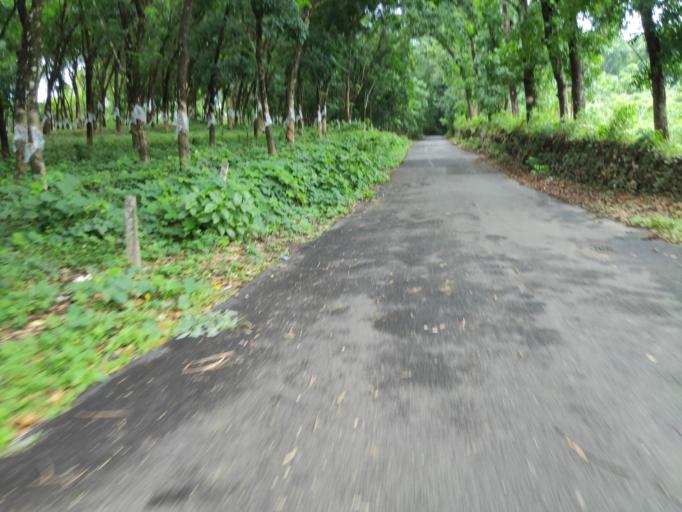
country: IN
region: Kerala
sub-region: Malappuram
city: Manjeri
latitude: 11.2350
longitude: 76.2501
